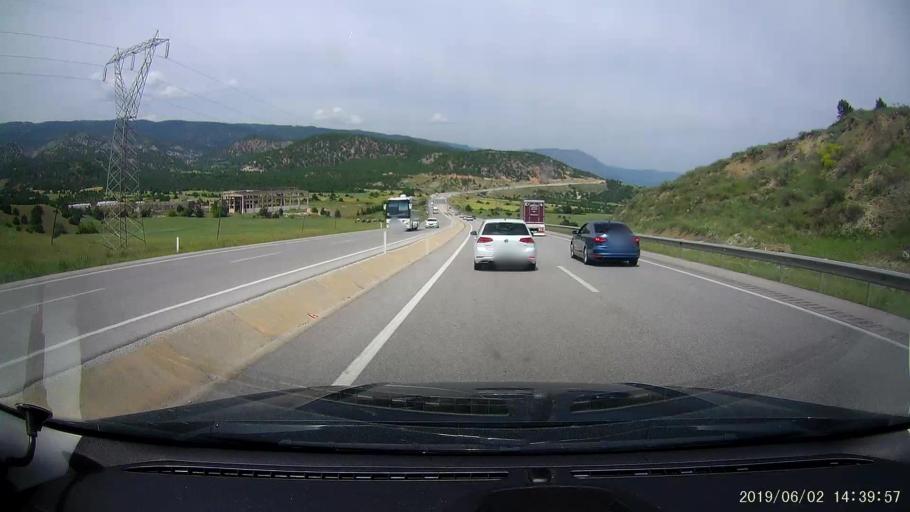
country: TR
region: Corum
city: Hacihamza
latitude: 41.0761
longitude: 34.3106
